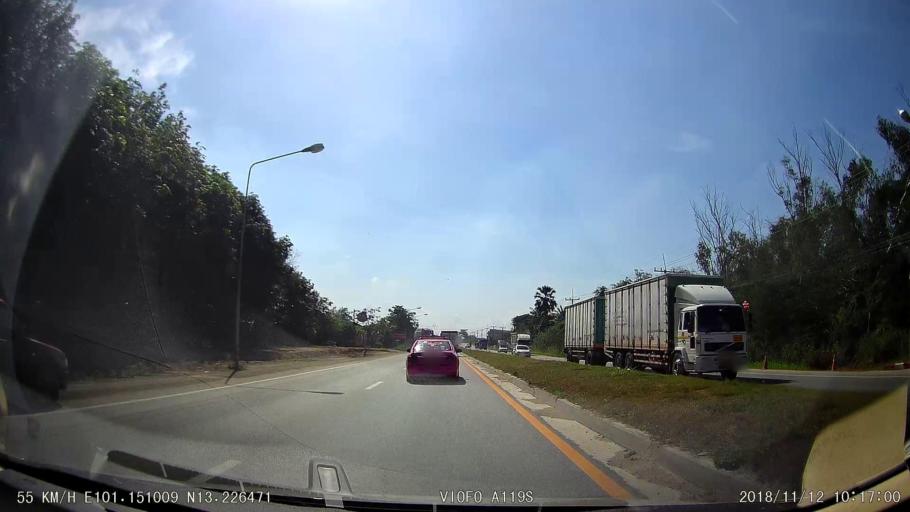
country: TH
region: Chon Buri
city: Ban Bueng
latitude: 13.2261
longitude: 101.1511
